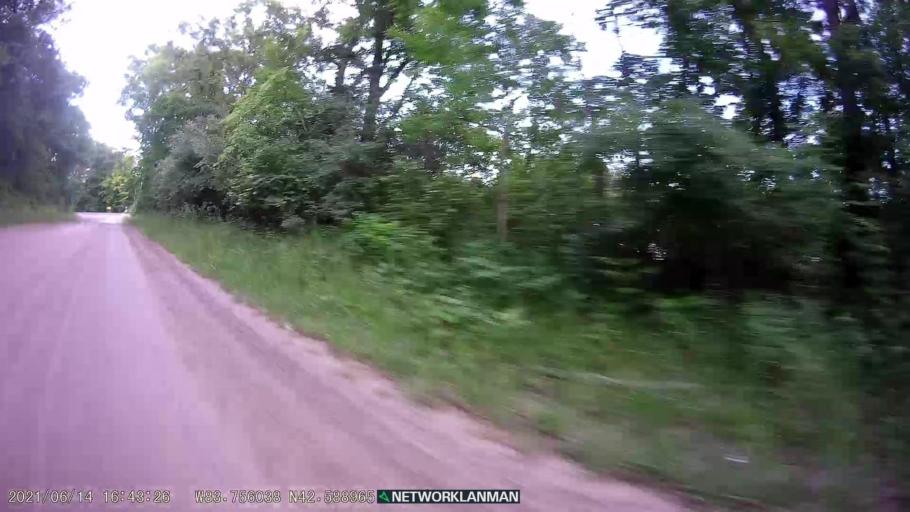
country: US
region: Michigan
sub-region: Livingston County
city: Brighton
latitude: 42.5888
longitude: -83.7556
